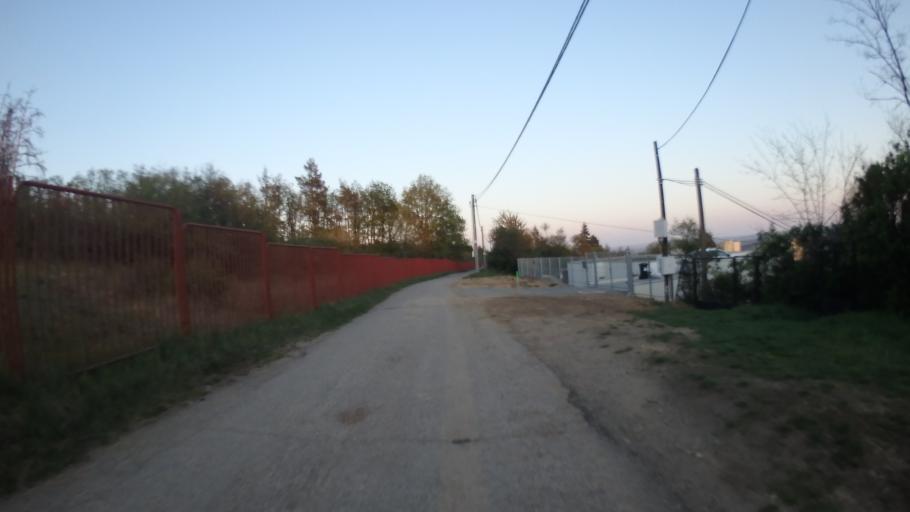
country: CZ
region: South Moravian
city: Ostopovice
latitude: 49.1838
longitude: 16.5488
